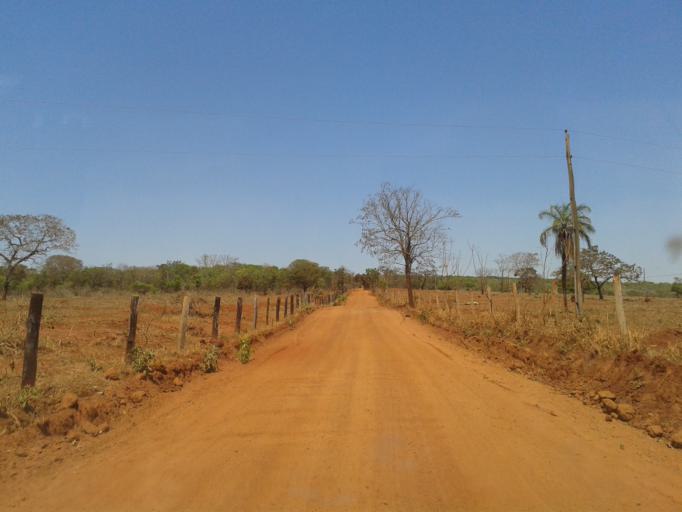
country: BR
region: Minas Gerais
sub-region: Ituiutaba
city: Ituiutaba
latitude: -19.0688
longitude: -49.3201
